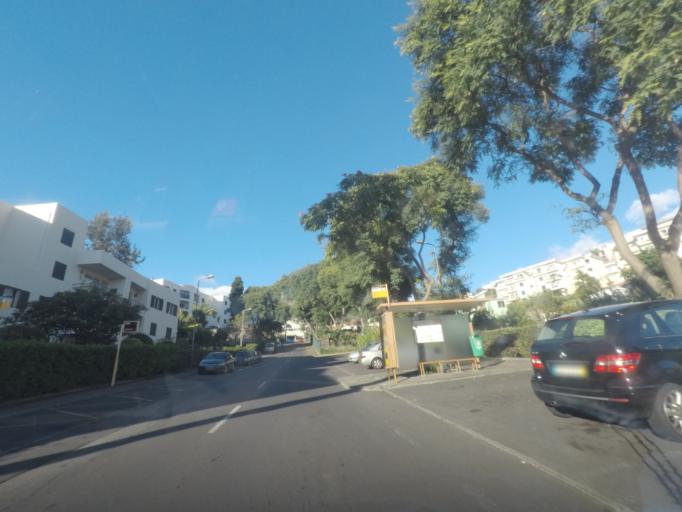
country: PT
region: Madeira
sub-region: Funchal
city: Nossa Senhora do Monte
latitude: 32.6640
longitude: -16.9284
